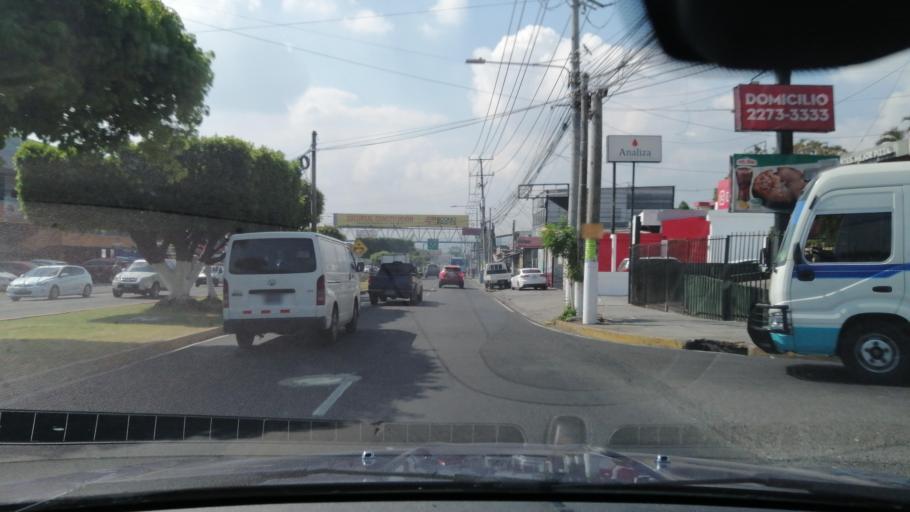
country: SV
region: San Salvador
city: Mejicanos
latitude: 13.7221
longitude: -89.2223
